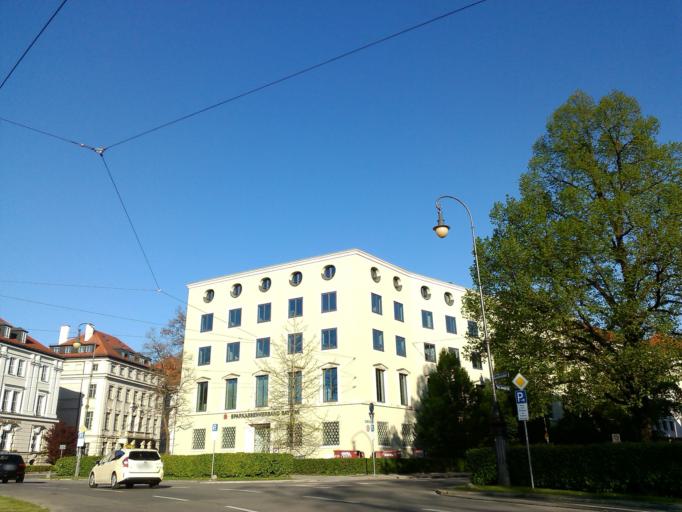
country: DE
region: Bavaria
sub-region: Upper Bavaria
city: Munich
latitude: 48.1444
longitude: 11.5691
